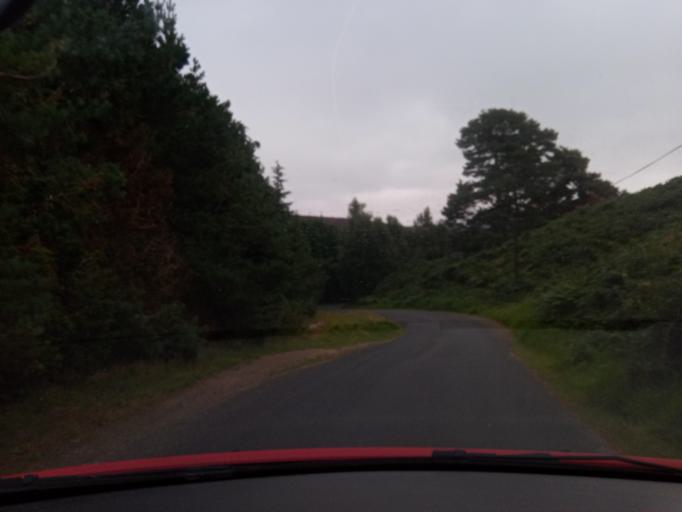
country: GB
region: England
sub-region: Northumberland
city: Rothbury
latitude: 55.2934
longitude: -2.0445
